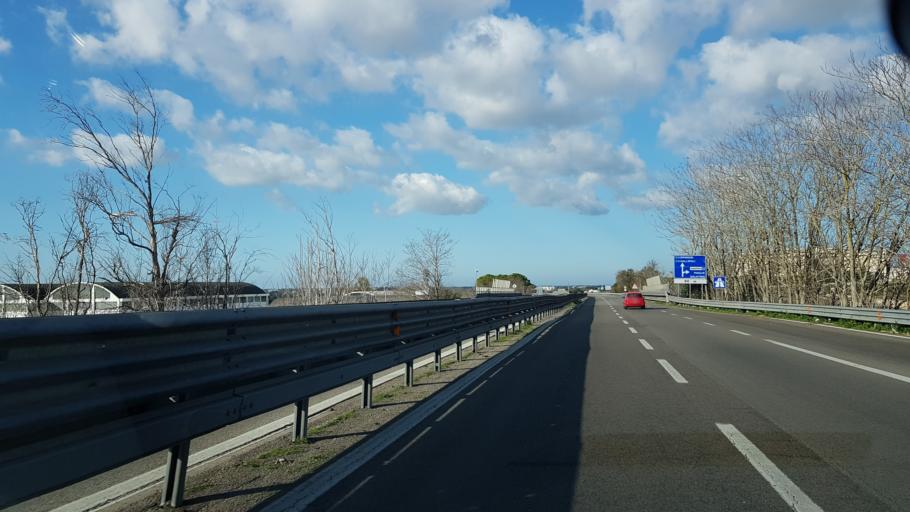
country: IT
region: Apulia
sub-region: Provincia di Lecce
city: Castromediano
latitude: 40.3251
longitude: 18.1661
